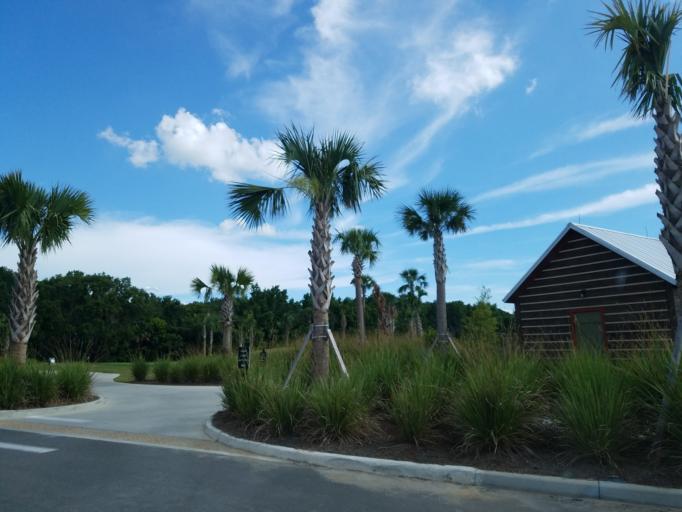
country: US
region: Florida
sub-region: Sumter County
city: Lake Panasoffkee
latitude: 28.7961
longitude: -82.0438
